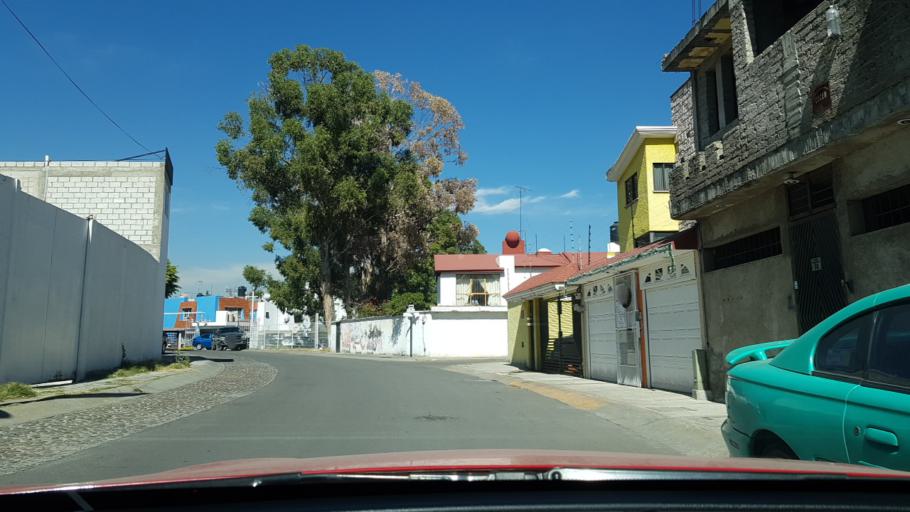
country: MX
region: Mexico
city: Cuautitlan Izcalli
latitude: 19.6403
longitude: -99.1981
